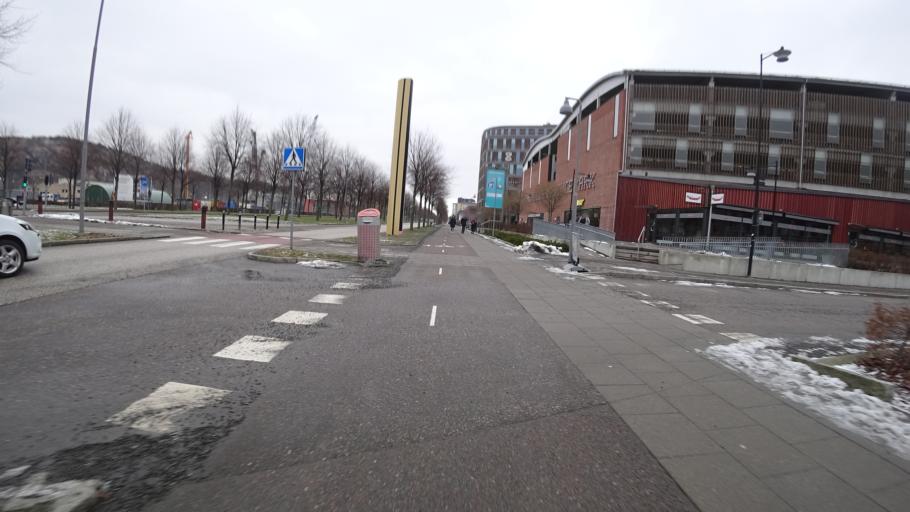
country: SE
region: Vaestra Goetaland
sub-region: Goteborg
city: Majorna
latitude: 57.7081
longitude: 11.9387
